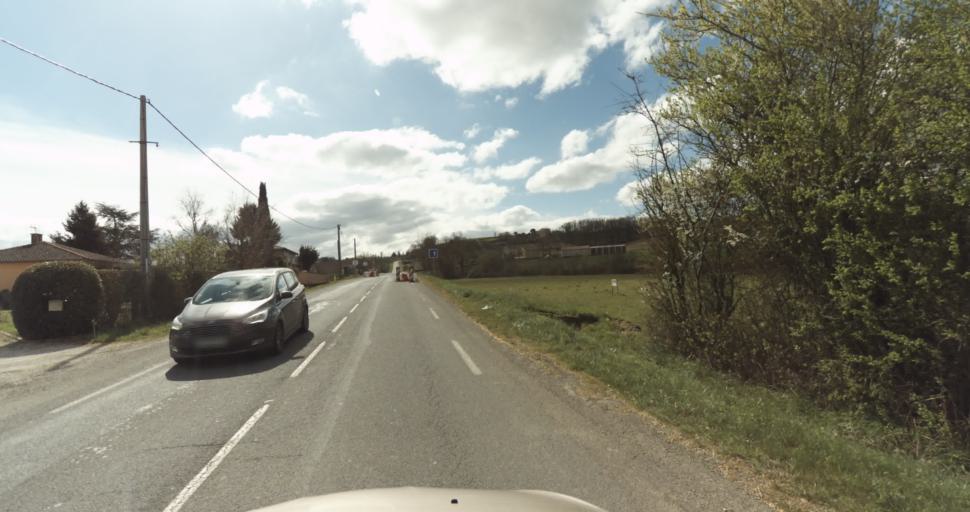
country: FR
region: Midi-Pyrenees
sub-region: Departement du Tarn
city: Puygouzon
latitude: 43.8884
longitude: 2.1536
